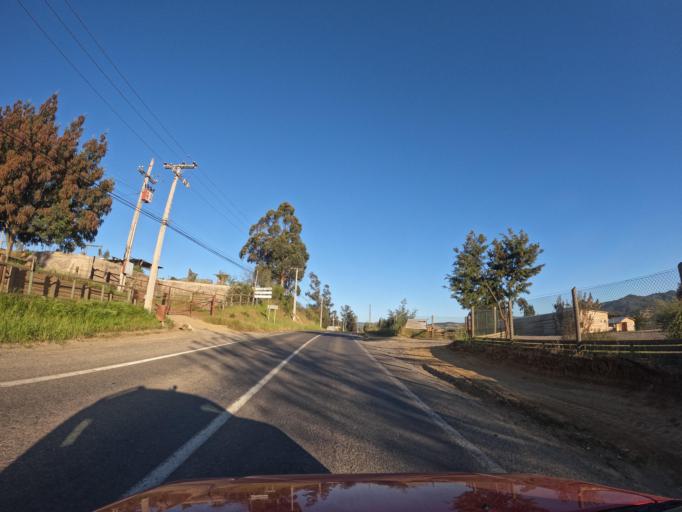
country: CL
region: Maule
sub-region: Provincia de Talca
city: Talca
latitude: -34.9958
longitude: -71.9697
